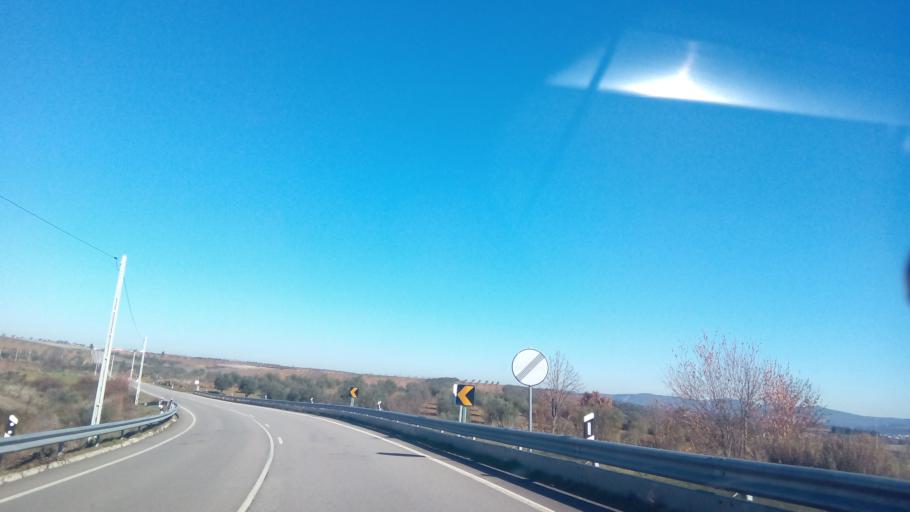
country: PT
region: Braganca
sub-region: Vimioso
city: Vimioso
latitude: 41.6191
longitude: -6.6086
